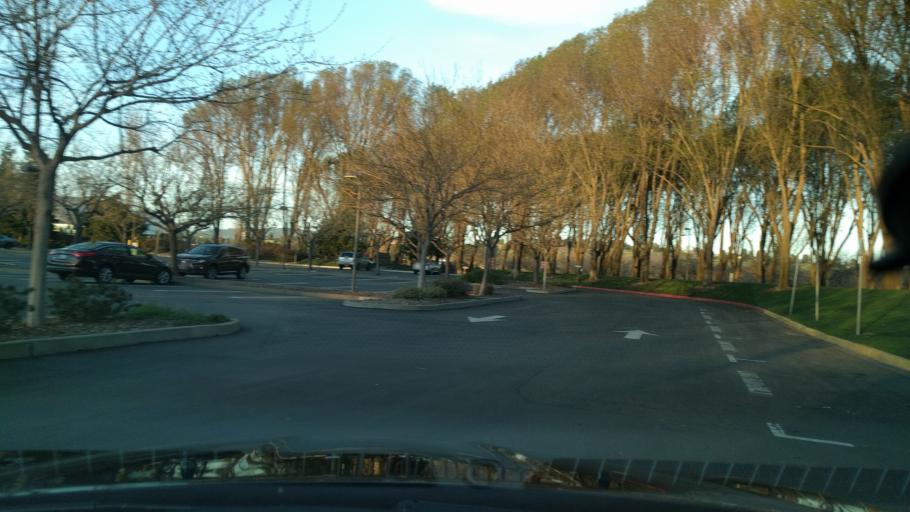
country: US
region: California
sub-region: Contra Costa County
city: San Ramon
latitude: 37.7603
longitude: -121.9606
